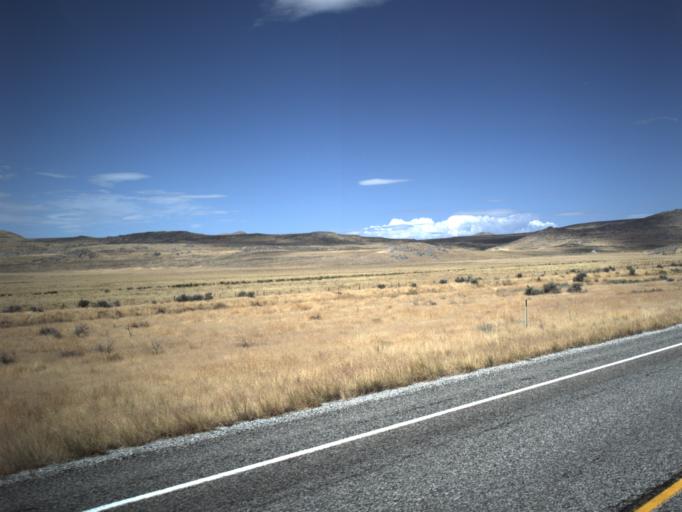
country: US
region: Utah
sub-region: Box Elder County
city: Tremonton
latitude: 41.6440
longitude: -112.4304
